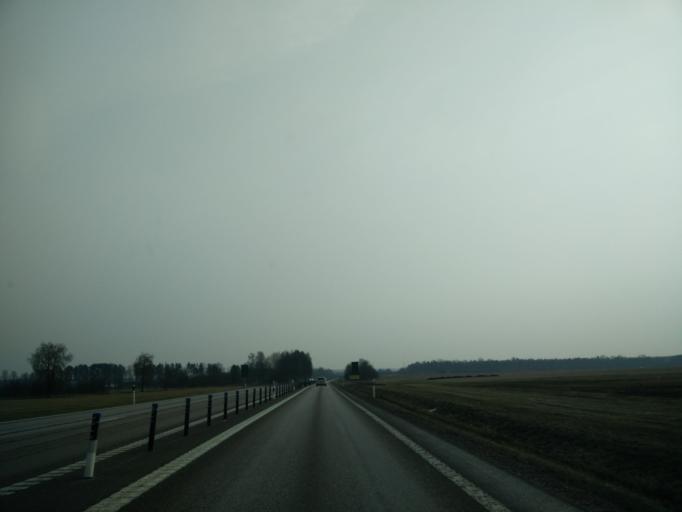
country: SE
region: Vaermland
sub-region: Karlstads Kommun
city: Karlstad
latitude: 59.4373
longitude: 13.4145
